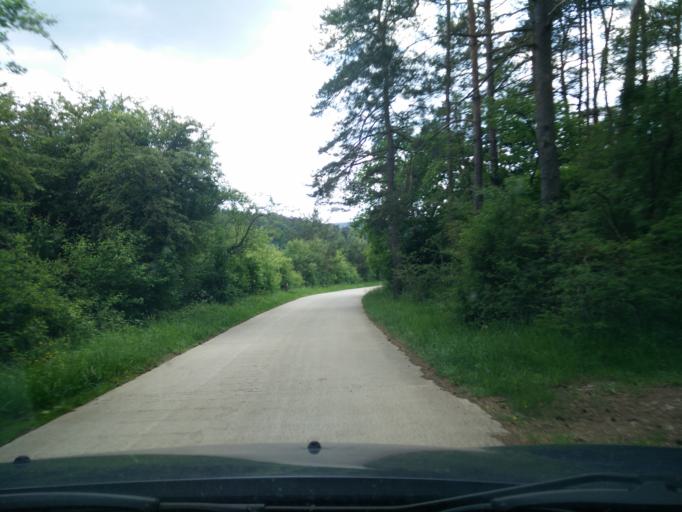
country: FR
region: Champagne-Ardenne
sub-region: Departement des Ardennes
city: Vireux-Molhain
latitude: 50.0817
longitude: 4.6167
